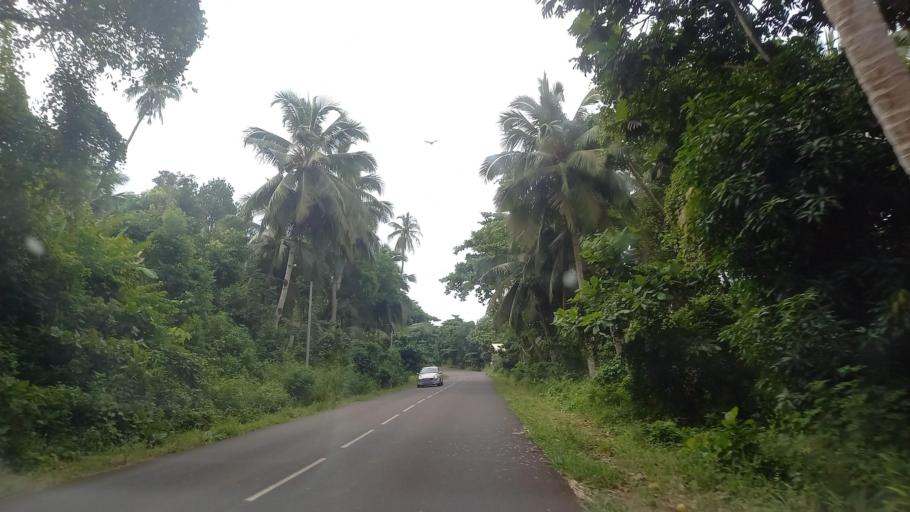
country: YT
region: Boueni
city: Boueni
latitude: -12.9176
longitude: 45.1018
